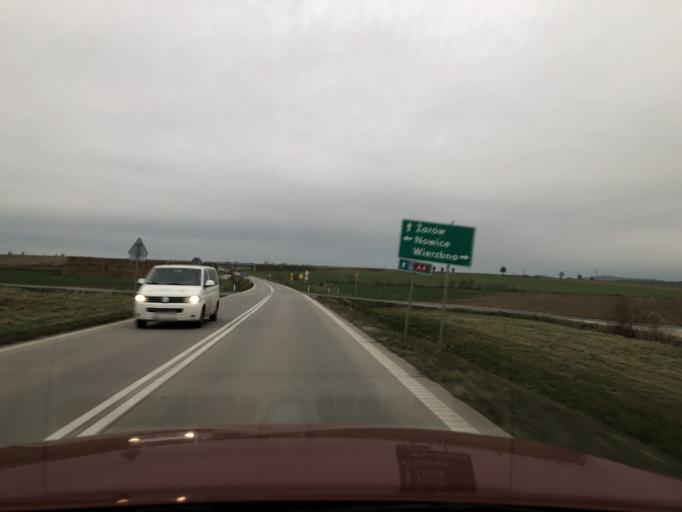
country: PL
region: Lower Silesian Voivodeship
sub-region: Powiat swidnicki
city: Zarow
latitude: 50.9091
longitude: 16.4811
